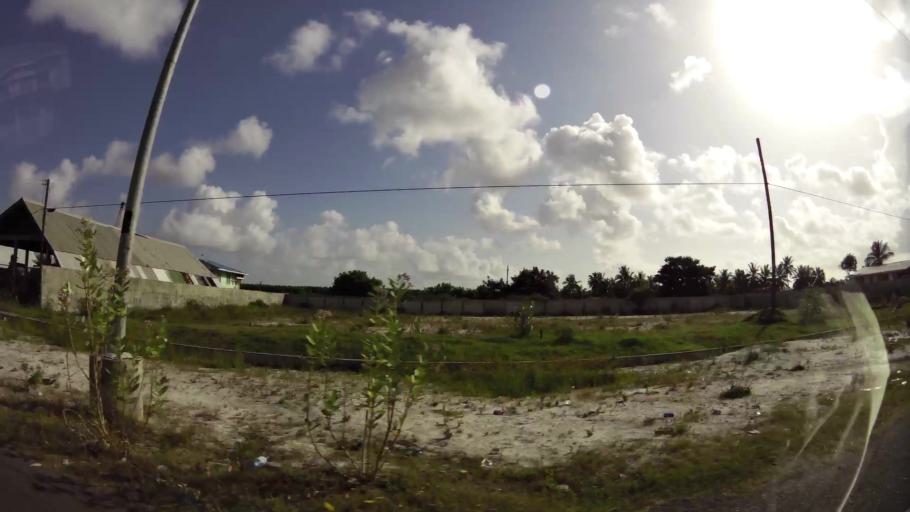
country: GY
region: Demerara-Mahaica
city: Georgetown
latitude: 6.8146
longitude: -58.0698
